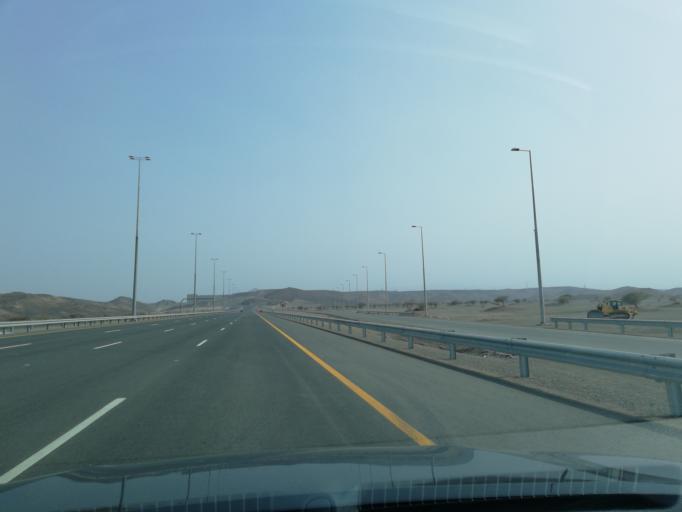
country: OM
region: Al Batinah
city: Al Liwa'
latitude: 24.3658
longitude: 56.5525
